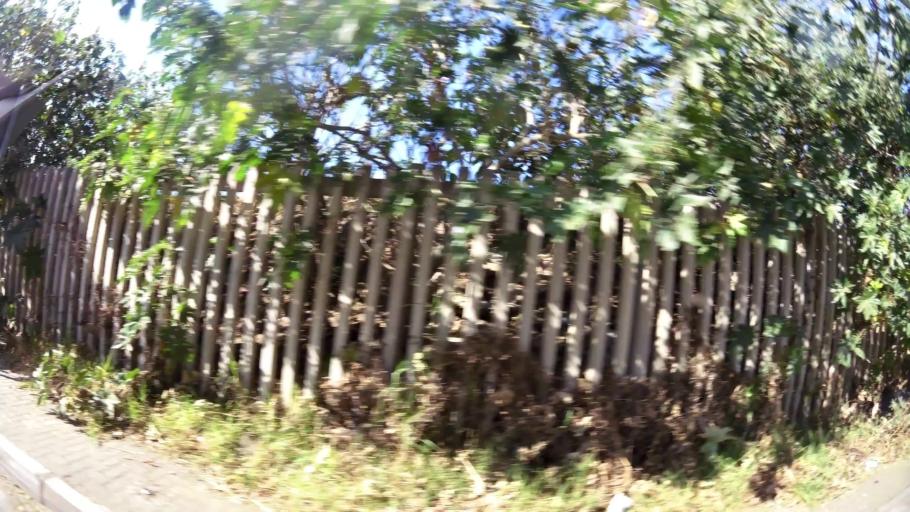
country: ZA
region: Gauteng
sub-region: City of Johannesburg Metropolitan Municipality
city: Johannesburg
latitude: -26.1811
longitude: 27.9671
